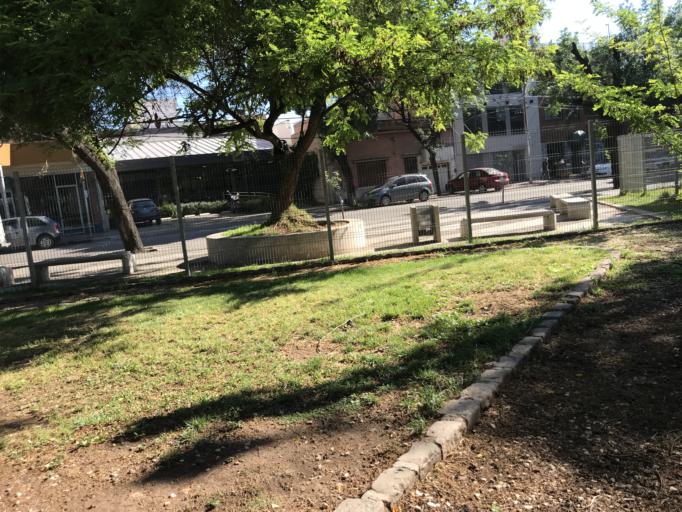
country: AR
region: Mendoza
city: Mendoza
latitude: -32.8879
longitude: -68.8321
